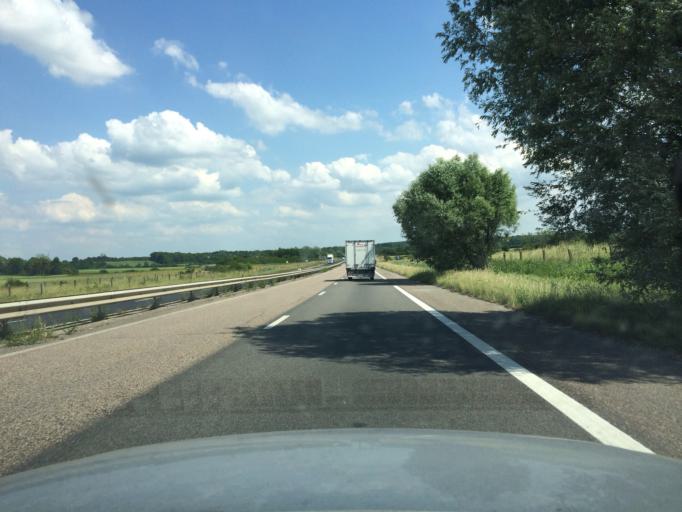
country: FR
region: Lorraine
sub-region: Departement de Meurthe-et-Moselle
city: Domgermain
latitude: 48.6539
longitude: 5.8462
